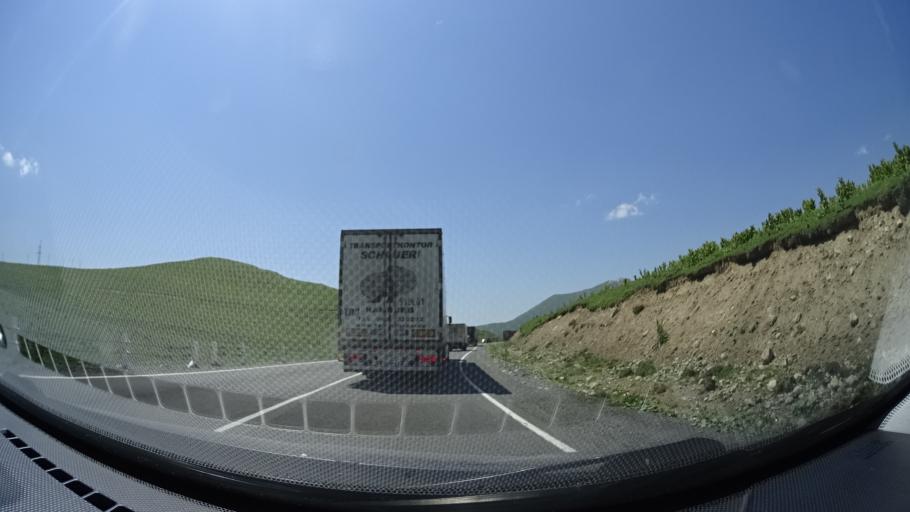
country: GE
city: Gudauri
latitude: 42.5030
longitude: 44.4545
